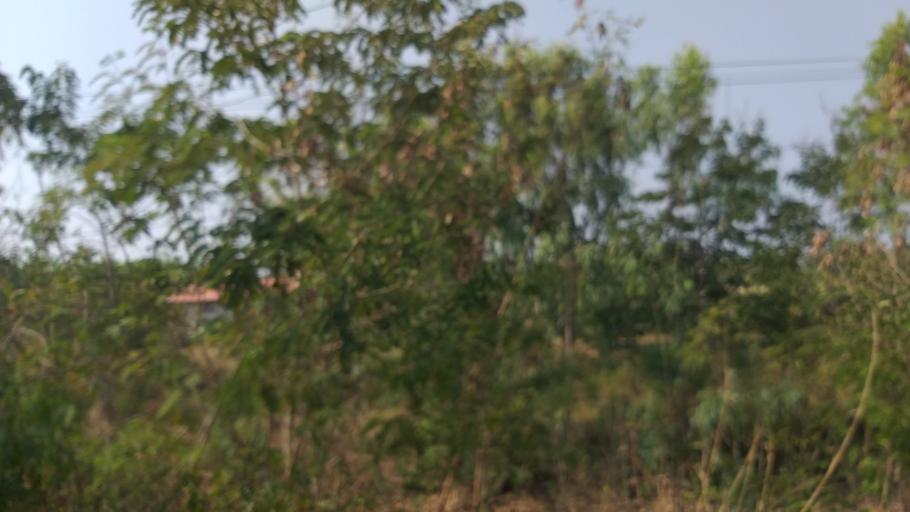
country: TH
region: Changwat Udon Thani
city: Thung Fon
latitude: 17.5332
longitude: 103.2273
